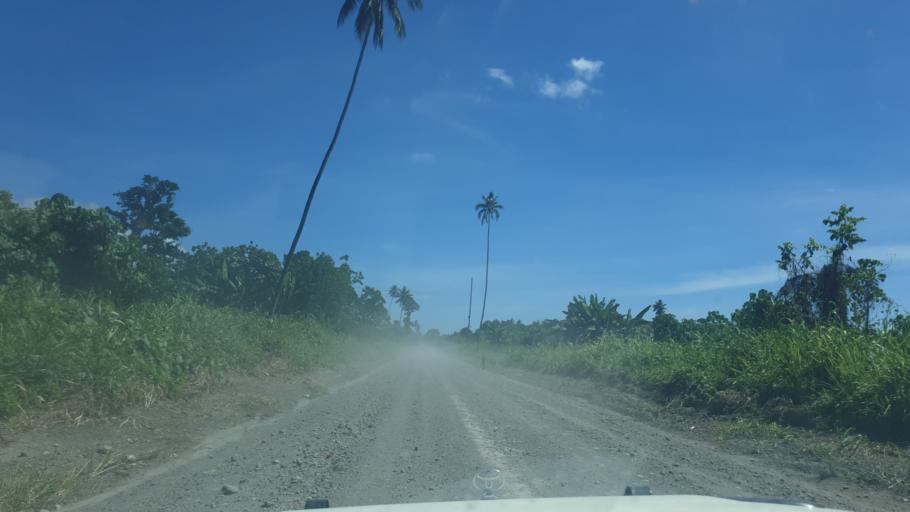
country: PG
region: Bougainville
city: Arawa
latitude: -5.9732
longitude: 155.3470
